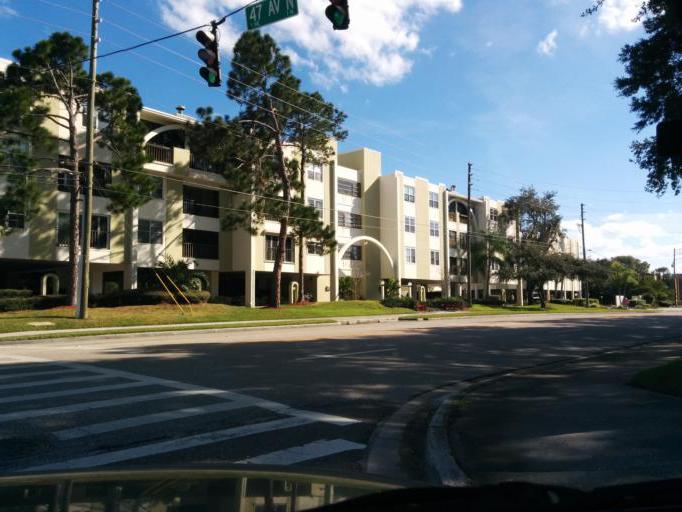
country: US
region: Florida
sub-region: Pinellas County
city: Lealman
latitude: 27.8148
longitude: -82.6346
